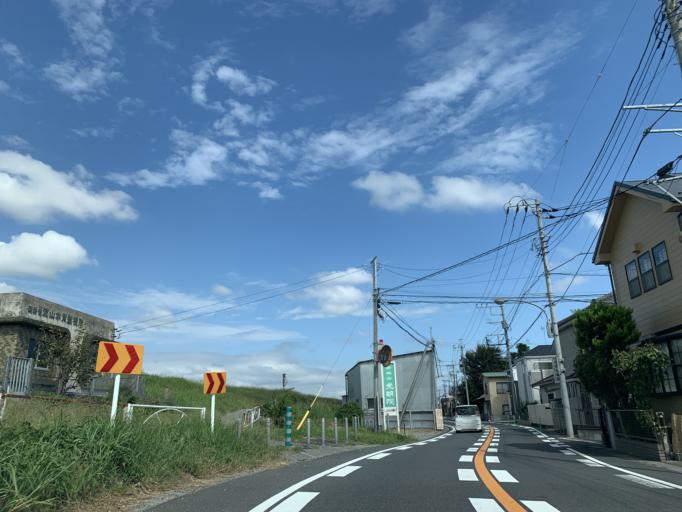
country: JP
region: Chiba
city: Nagareyama
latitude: 35.8495
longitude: 139.8943
